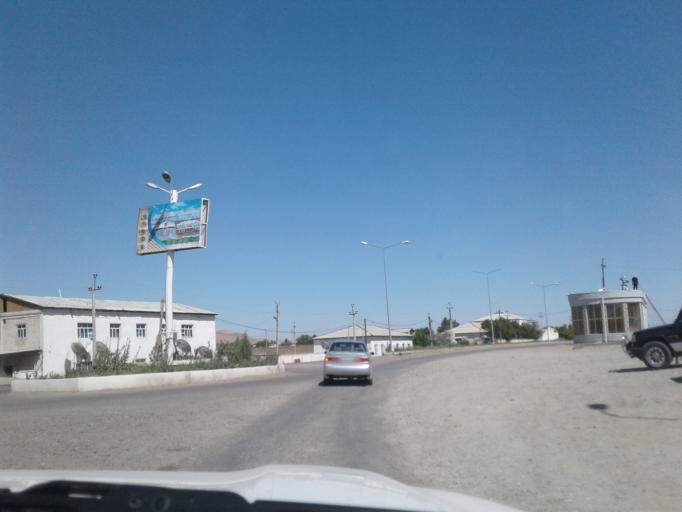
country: AF
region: Badghis
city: Bala Murghab
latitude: 35.9496
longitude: 62.9267
